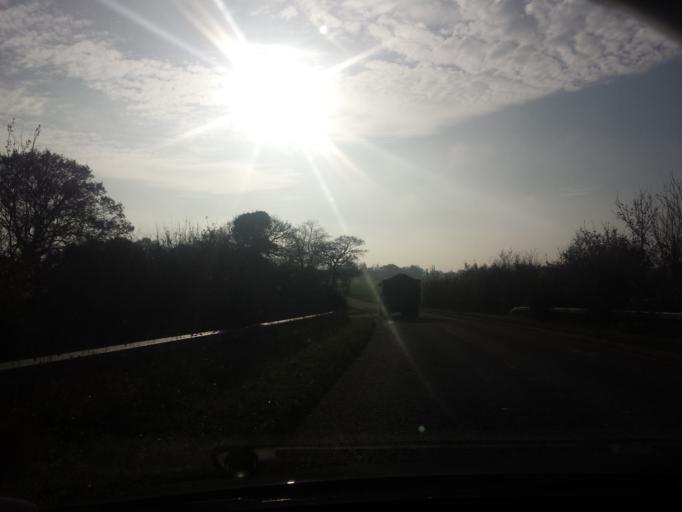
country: GB
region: England
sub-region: Essex
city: Little Clacton
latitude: 51.8378
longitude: 1.1215
